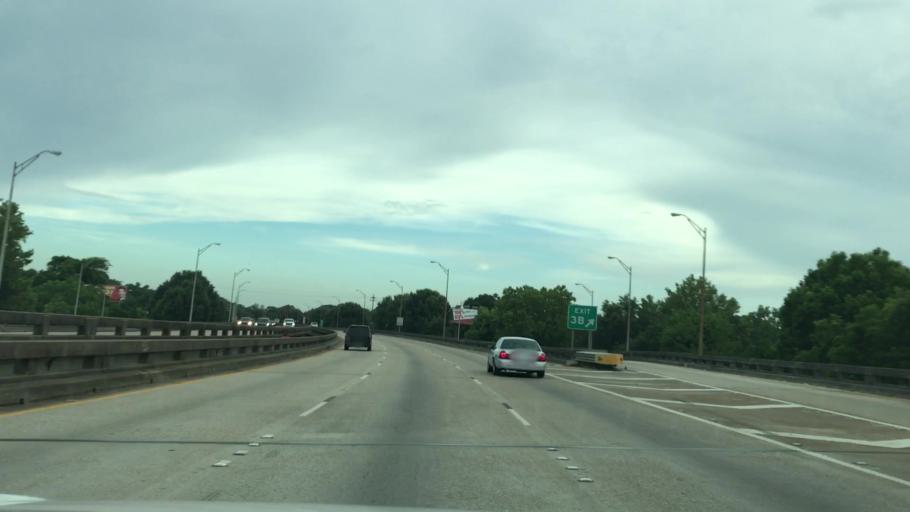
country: US
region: Louisiana
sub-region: East Baton Rouge Parish
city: Baton Rouge
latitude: 30.4879
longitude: -91.1663
